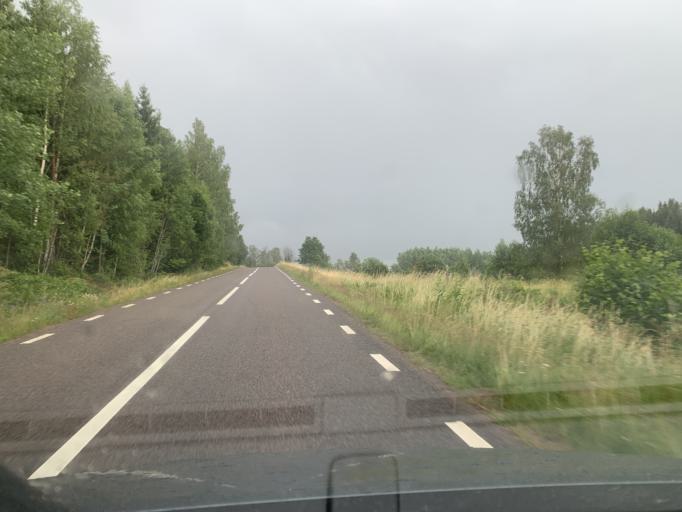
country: SE
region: Kalmar
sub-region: Vasterviks Kommun
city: Overum
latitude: 58.0018
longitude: 16.1760
